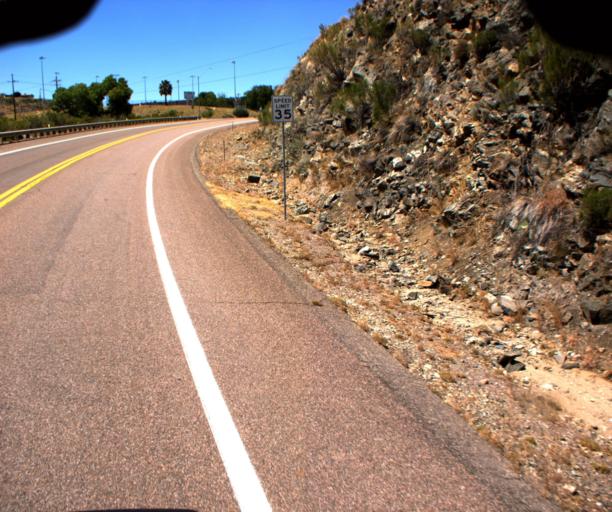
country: US
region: Arizona
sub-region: Yavapai County
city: Bagdad
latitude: 34.5662
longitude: -113.1748
